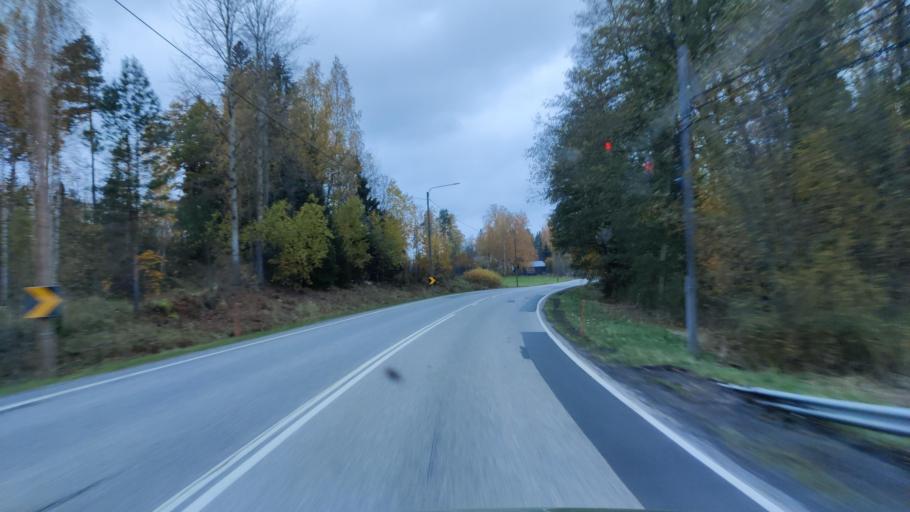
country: FI
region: Uusimaa
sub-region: Helsinki
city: Vihti
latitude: 60.3357
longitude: 24.1999
